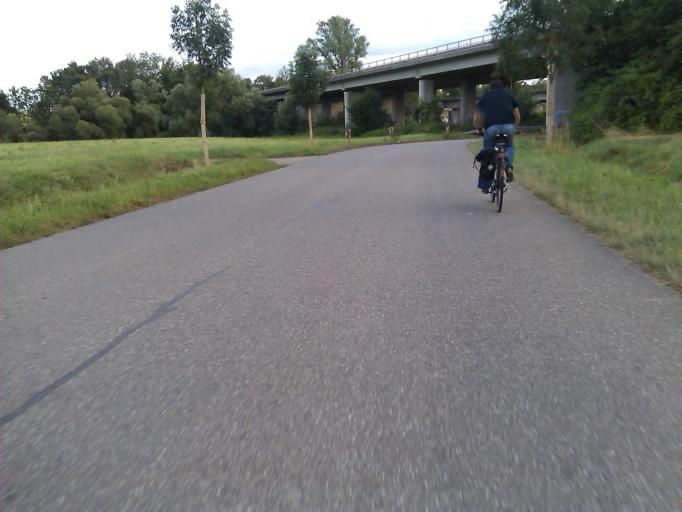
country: DE
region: Baden-Wuerttemberg
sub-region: Regierungsbezirk Stuttgart
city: Untereisesheim
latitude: 49.2249
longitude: 9.2090
